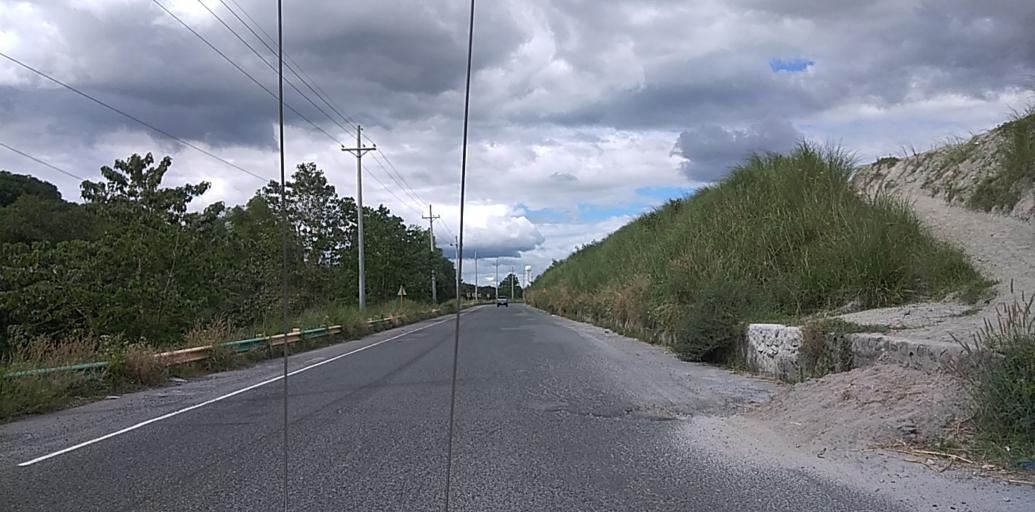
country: PH
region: Central Luzon
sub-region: Province of Pampanga
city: Dolores
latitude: 15.1045
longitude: 120.5217
